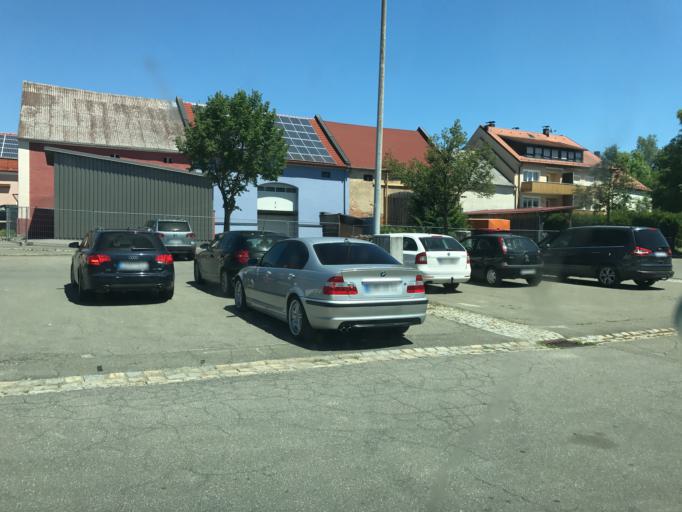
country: DE
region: Bavaria
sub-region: Upper Palatinate
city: Waldmunchen
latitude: 49.3761
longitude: 12.7026
